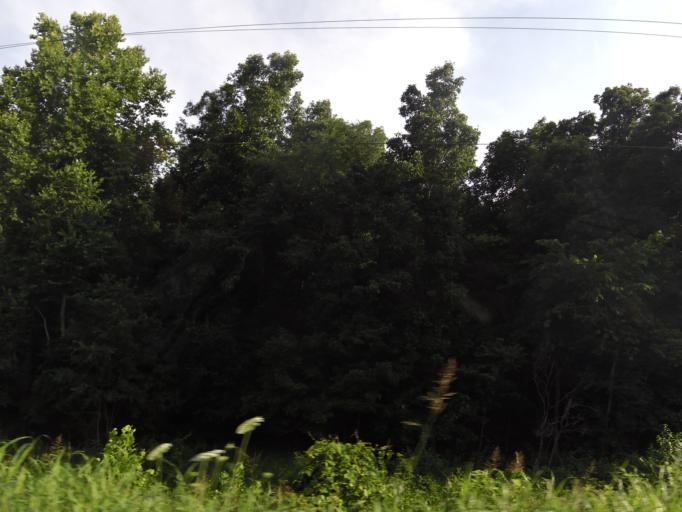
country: US
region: Tennessee
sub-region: Humphreys County
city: McEwen
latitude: 36.1019
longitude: -87.6124
